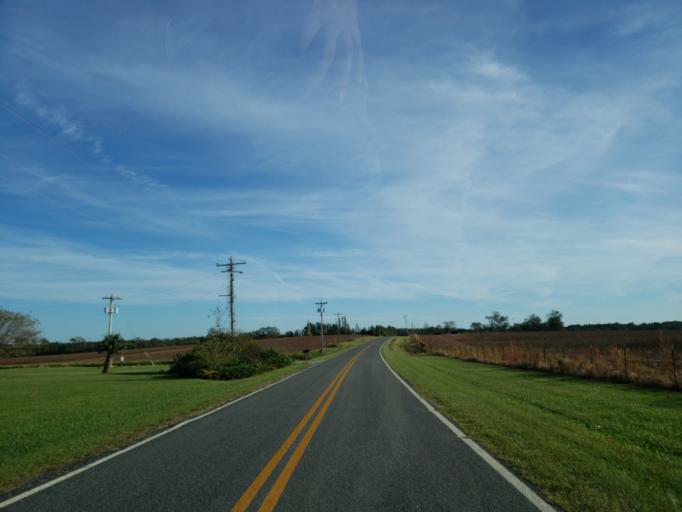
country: US
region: Georgia
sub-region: Dooly County
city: Vienna
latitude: 32.0420
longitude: -83.7543
